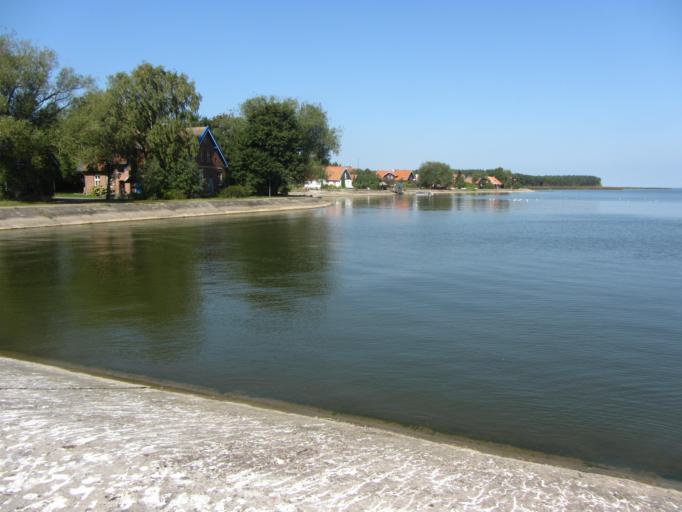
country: LT
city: Neringa
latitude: 55.3728
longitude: 21.0682
